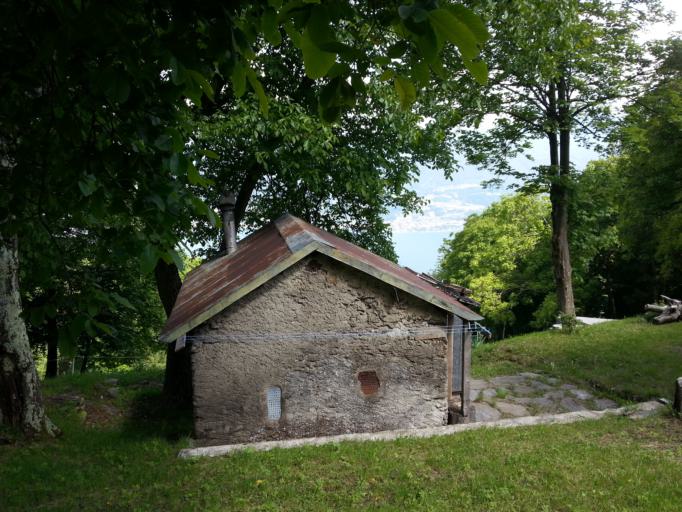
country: IT
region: Lombardy
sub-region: Provincia di Lecco
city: Introzzo
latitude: 46.1044
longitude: 9.3519
